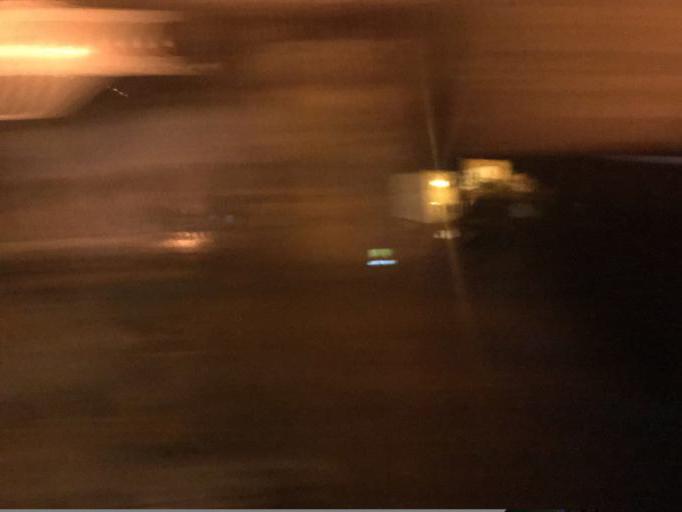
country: TR
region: Karabuk
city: Karabuk
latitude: 41.2180
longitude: 32.6579
